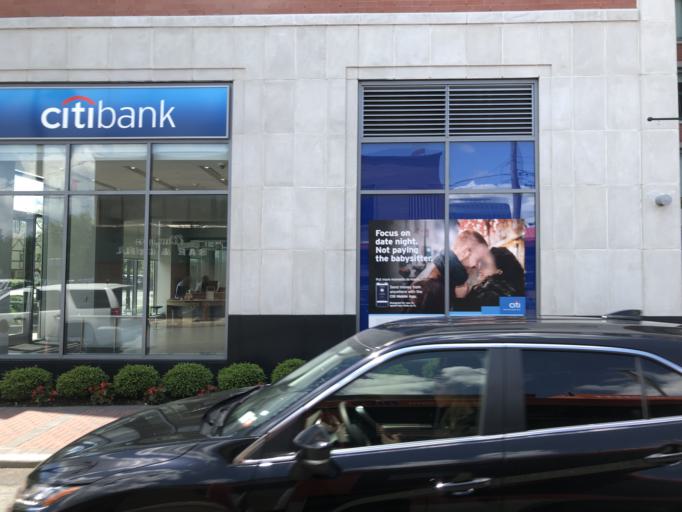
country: US
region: New York
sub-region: Nassau County
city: Mineola
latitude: 40.7390
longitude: -73.6406
